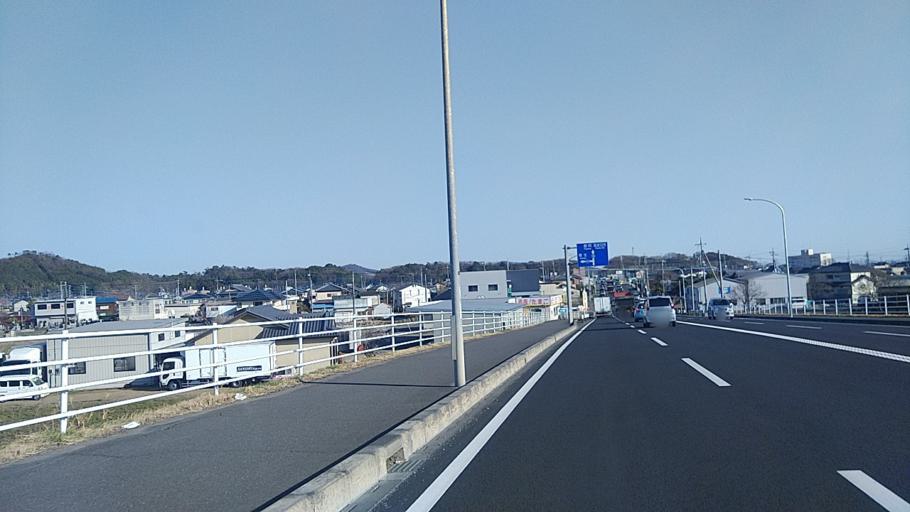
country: JP
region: Tochigi
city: Sano
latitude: 36.3383
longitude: 139.5769
